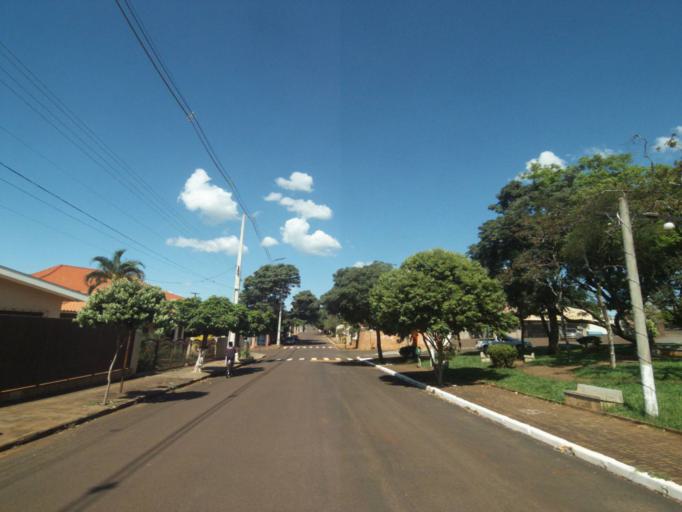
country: BR
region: Parana
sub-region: Sertanopolis
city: Sertanopolis
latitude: -23.0412
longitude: -50.8153
